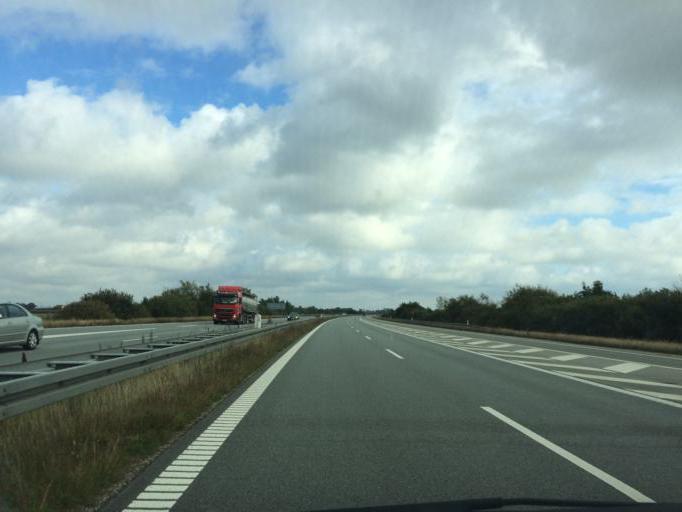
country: DK
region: North Denmark
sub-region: Bronderslev Kommune
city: Hjallerup
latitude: 57.1382
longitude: 10.0887
